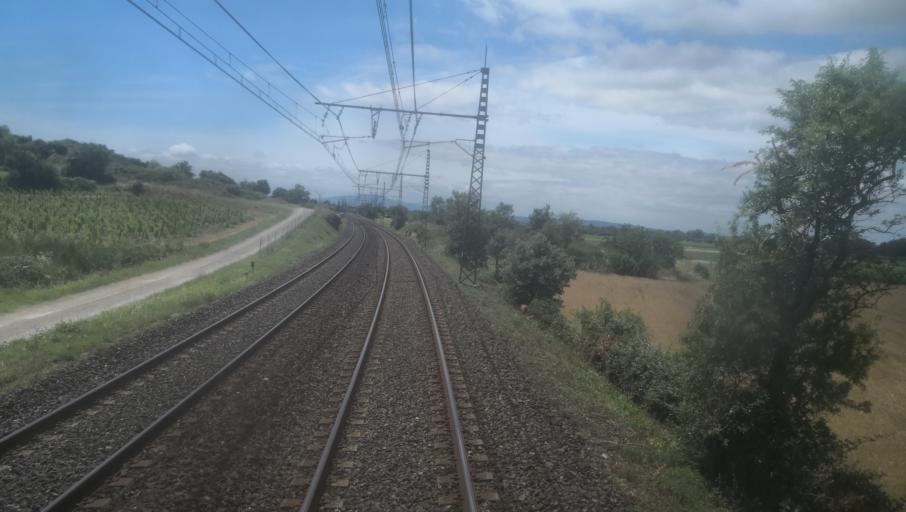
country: FR
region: Languedoc-Roussillon
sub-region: Departement de l'Aude
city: Nevian
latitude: 43.2130
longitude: 2.8837
